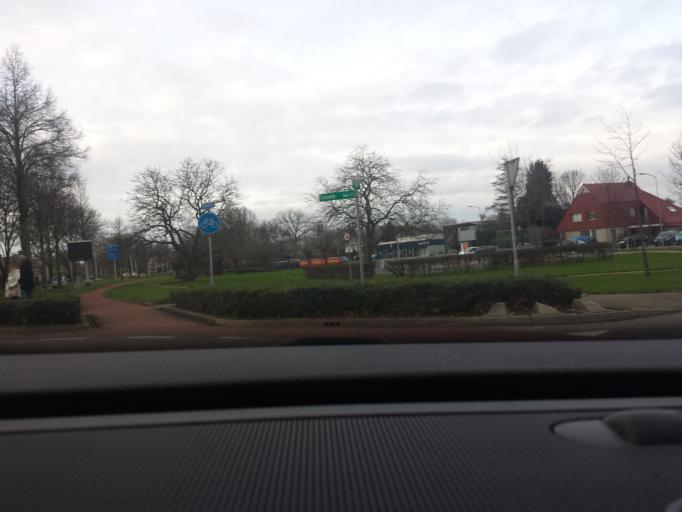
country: NL
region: Gelderland
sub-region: Gemeente Zevenaar
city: Zevenaar
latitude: 51.9338
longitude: 6.0835
